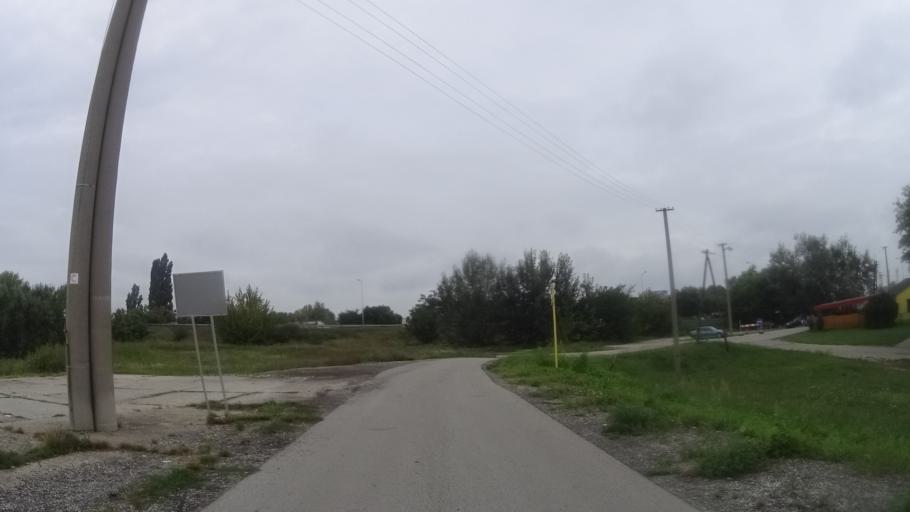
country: SK
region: Nitriansky
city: Komarno
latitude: 47.7610
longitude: 18.1458
